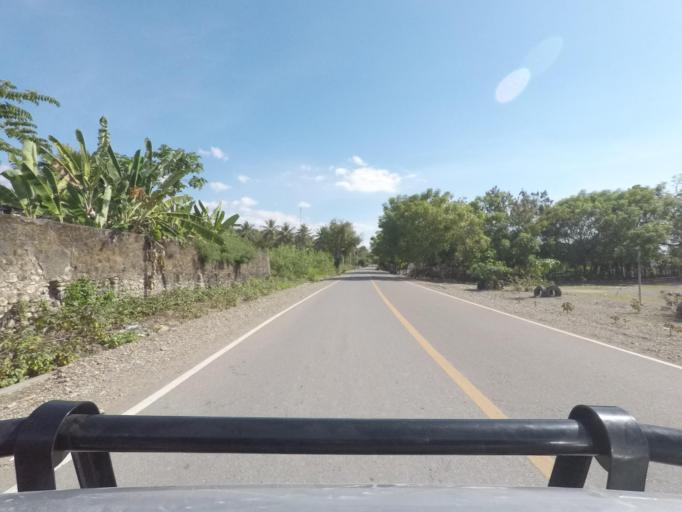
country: ID
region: East Nusa Tenggara
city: Atambua
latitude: -8.9463
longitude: 124.9723
